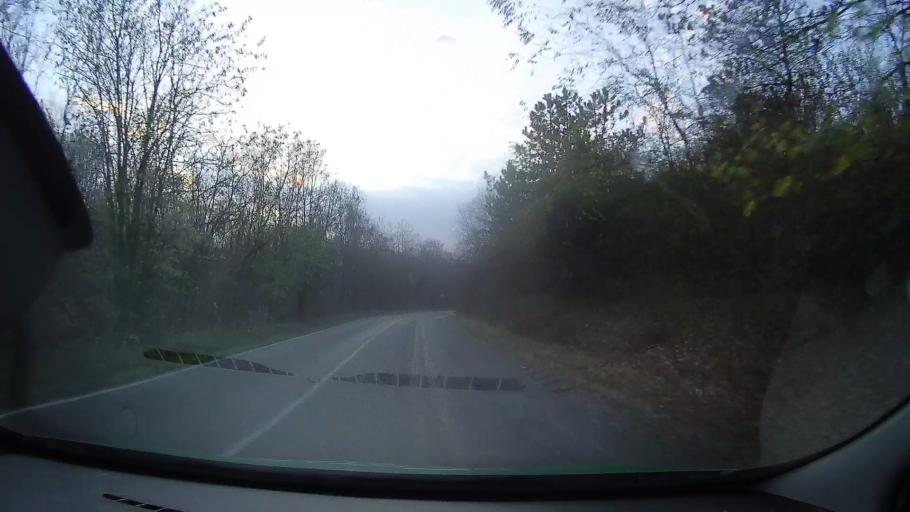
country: RO
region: Constanta
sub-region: Comuna Baneasa
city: Baneasa
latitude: 44.0874
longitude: 27.6610
